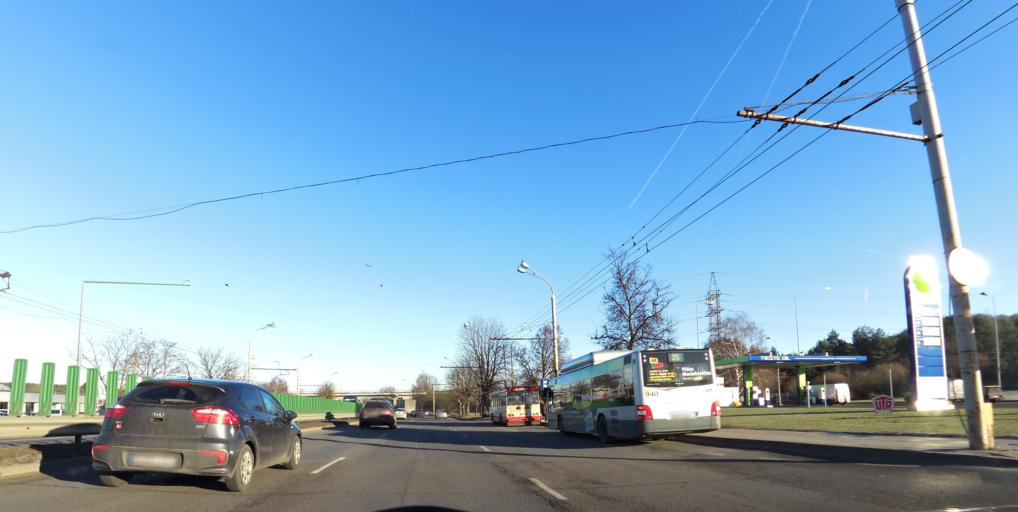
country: LT
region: Vilnius County
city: Lazdynai
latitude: 54.6443
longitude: 25.2059
